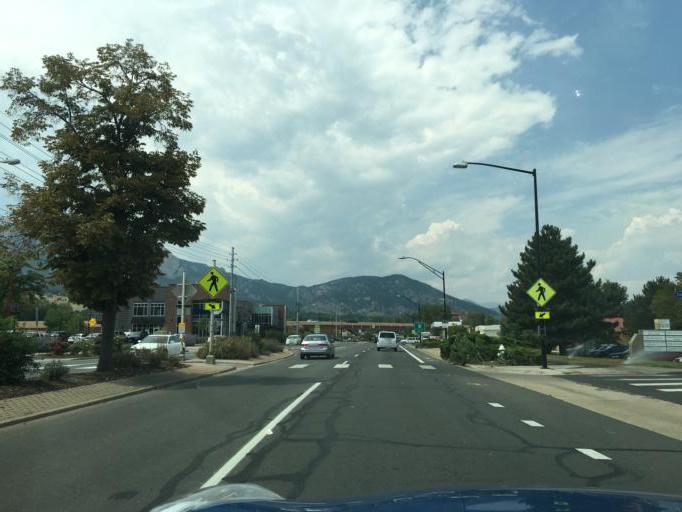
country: US
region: Colorado
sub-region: Boulder County
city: Boulder
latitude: 40.0001
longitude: -105.2544
